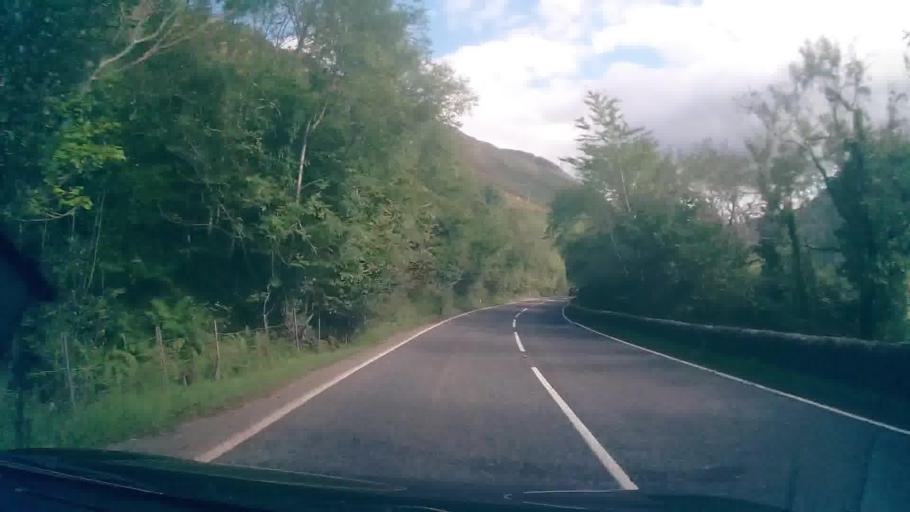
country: GB
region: Scotland
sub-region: Argyll and Bute
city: Oban
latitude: 56.4128
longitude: -5.1741
